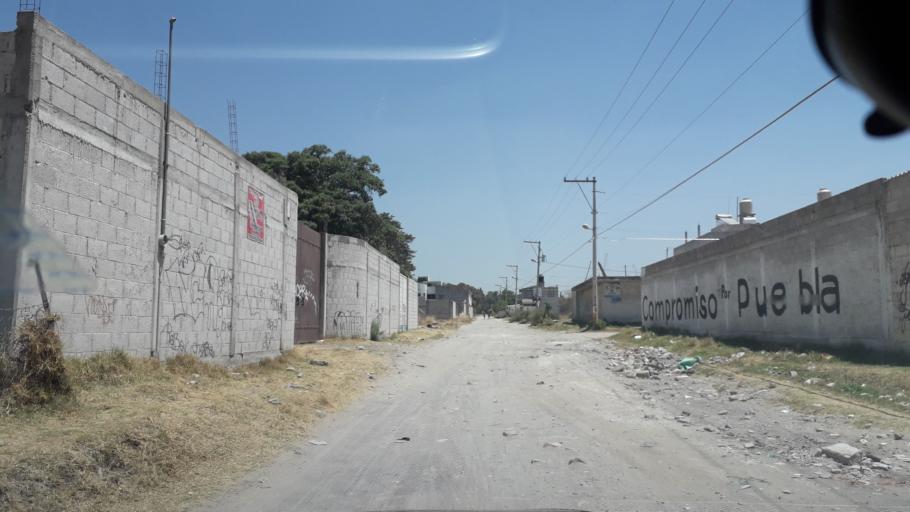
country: MX
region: Puebla
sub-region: Amozoc
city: Casa Blanca
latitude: 19.0557
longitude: -98.1196
